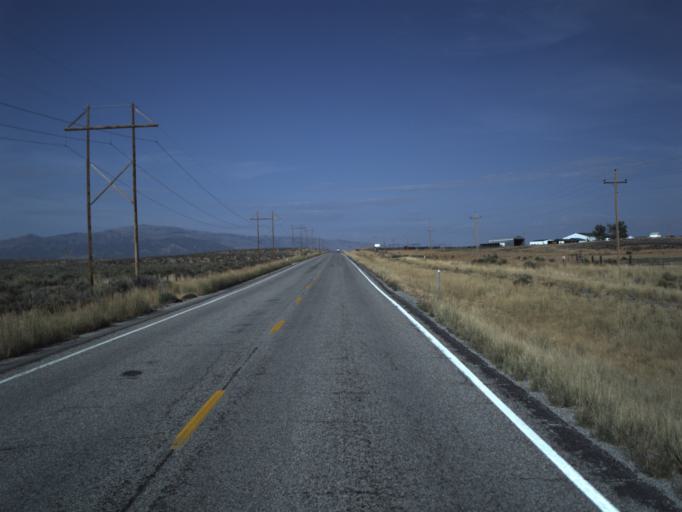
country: US
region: Idaho
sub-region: Oneida County
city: Malad City
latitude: 41.9659
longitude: -112.9874
